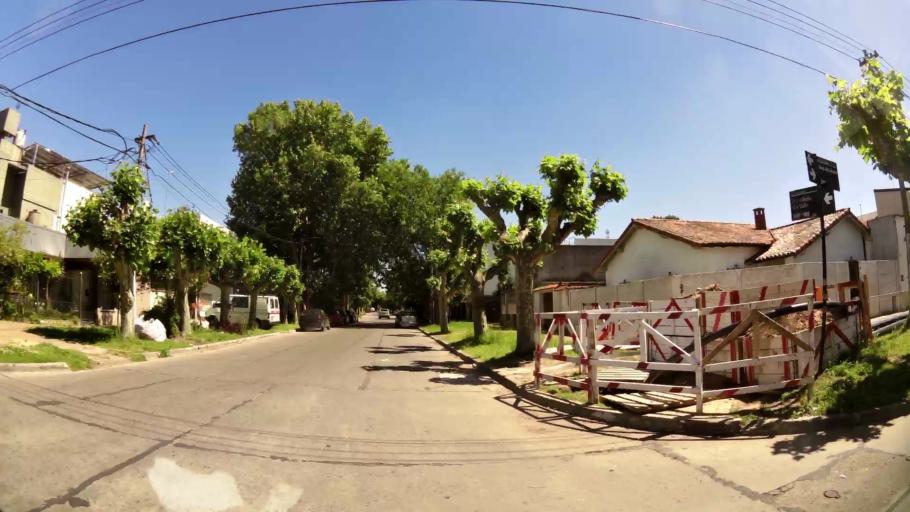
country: AR
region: Buenos Aires
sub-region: Partido de Quilmes
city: Quilmes
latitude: -34.7179
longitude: -58.2683
